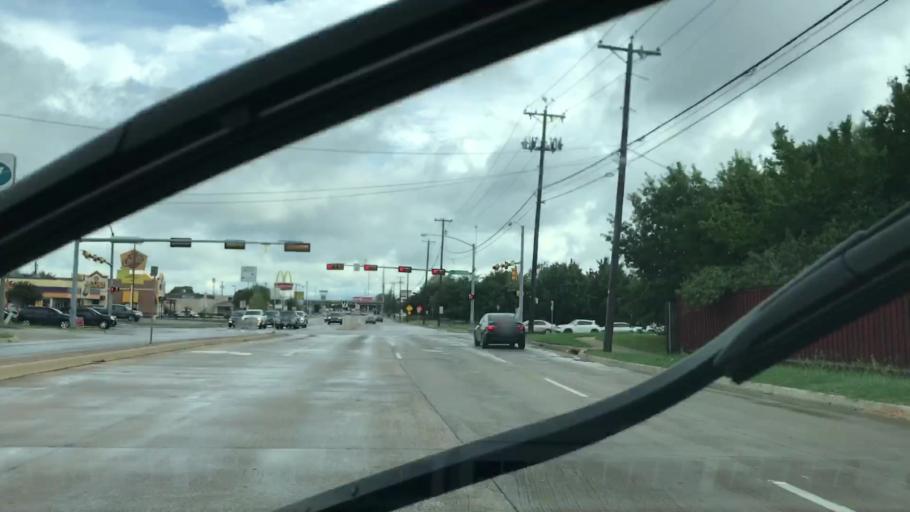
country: US
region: Texas
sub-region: Dallas County
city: Irving
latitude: 32.8423
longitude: -96.9765
